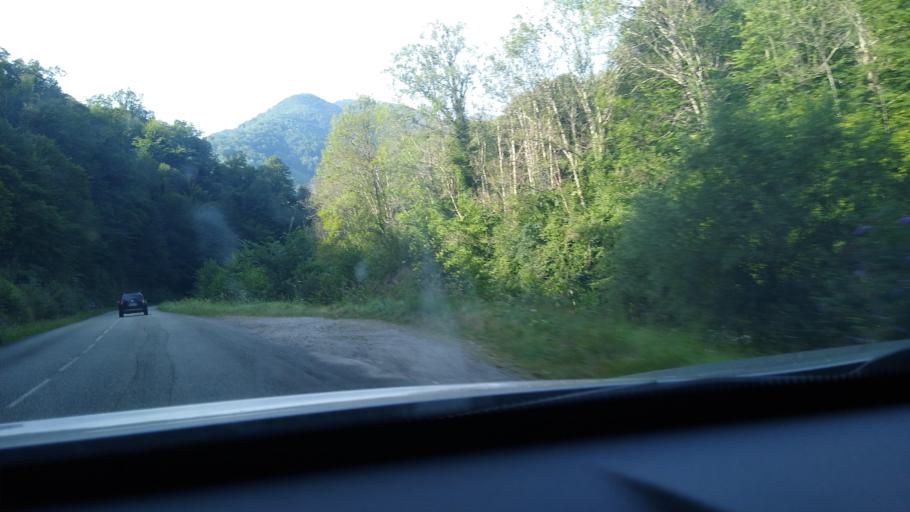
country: FR
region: Midi-Pyrenees
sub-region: Departement de l'Ariege
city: Saint-Girons
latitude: 42.8512
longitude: 1.1928
